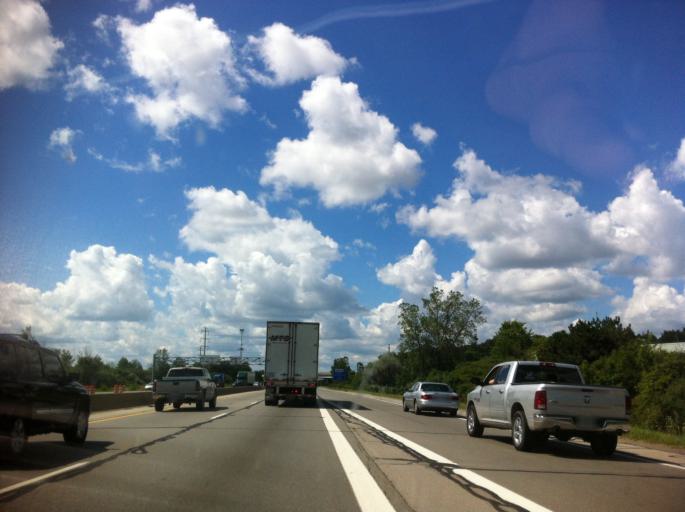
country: US
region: Michigan
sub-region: Washtenaw County
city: Ann Arbor
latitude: 42.2274
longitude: -83.6894
